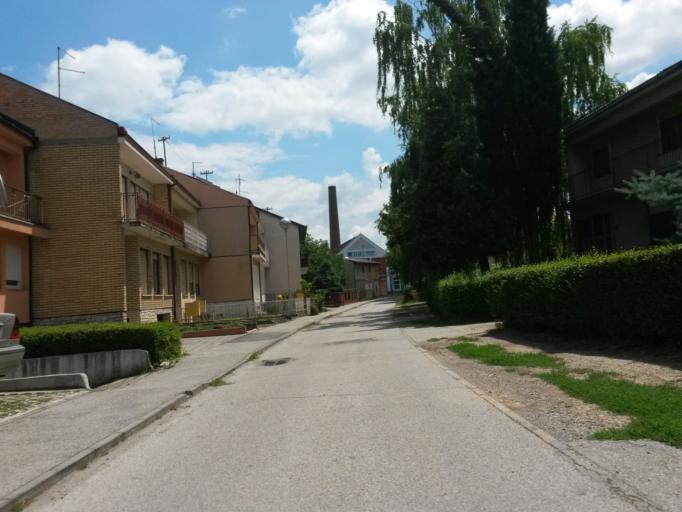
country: HR
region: Osjecko-Baranjska
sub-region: Grad Osijek
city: Osijek
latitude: 45.5551
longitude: 18.7305
